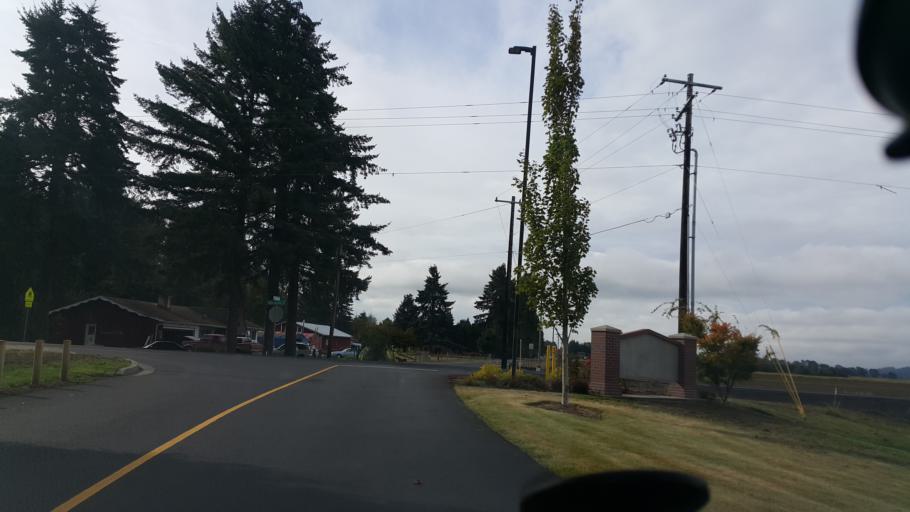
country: US
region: Washington
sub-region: Cowlitz County
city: Woodland
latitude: 45.9280
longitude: -122.7684
